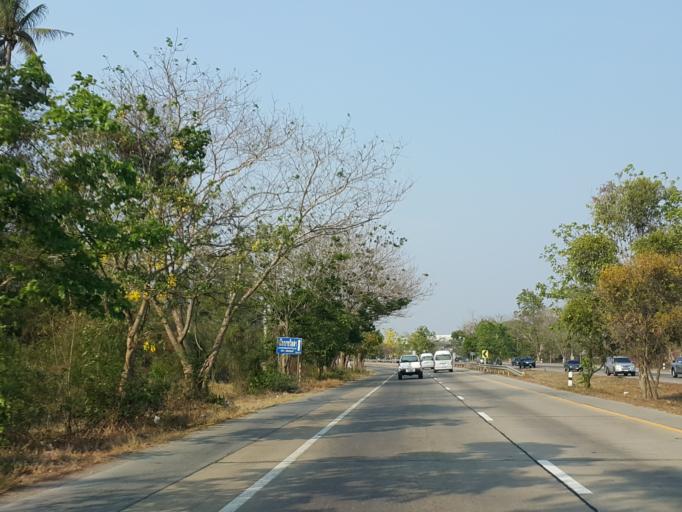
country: TH
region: Suphan Buri
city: Sam Chuk
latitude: 14.7901
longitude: 100.1026
